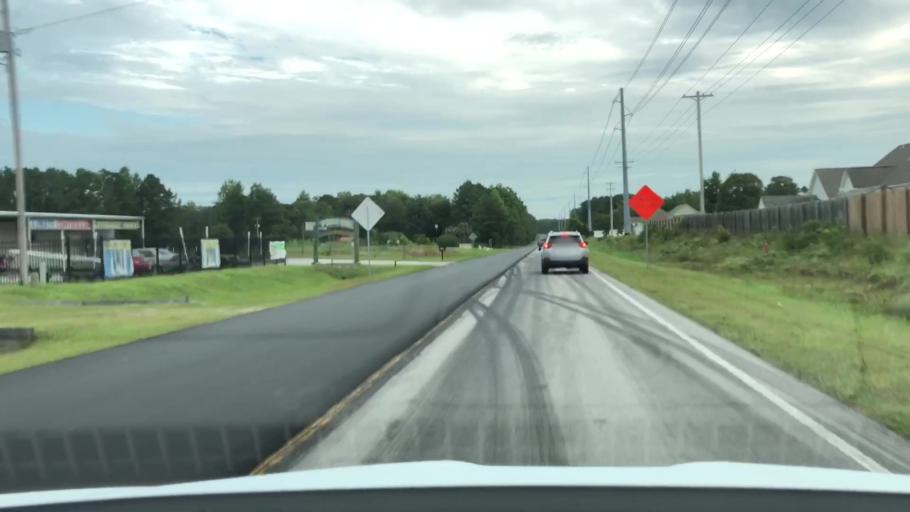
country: US
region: North Carolina
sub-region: Carteret County
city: Cape Carteret
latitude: 34.7600
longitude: -77.0947
